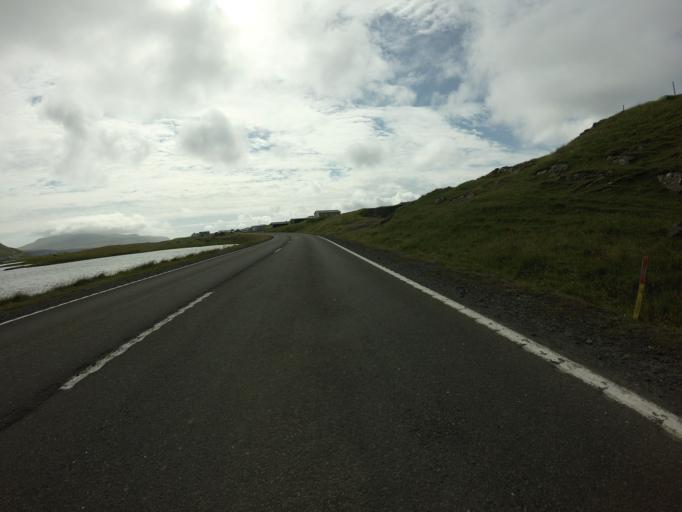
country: FO
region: Sandoy
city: Sandur
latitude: 61.8446
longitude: -6.8266
